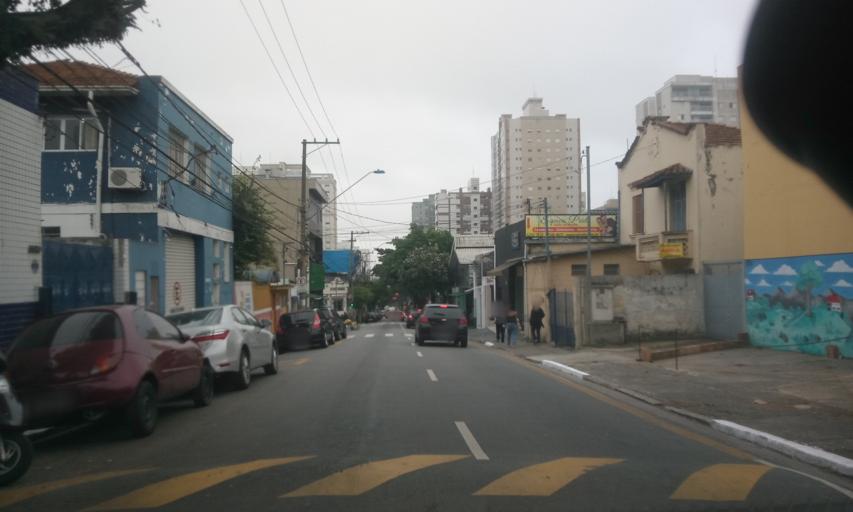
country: BR
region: Sao Paulo
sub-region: Sao Caetano Do Sul
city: Sao Caetano do Sul
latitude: -23.6237
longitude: -46.5694
